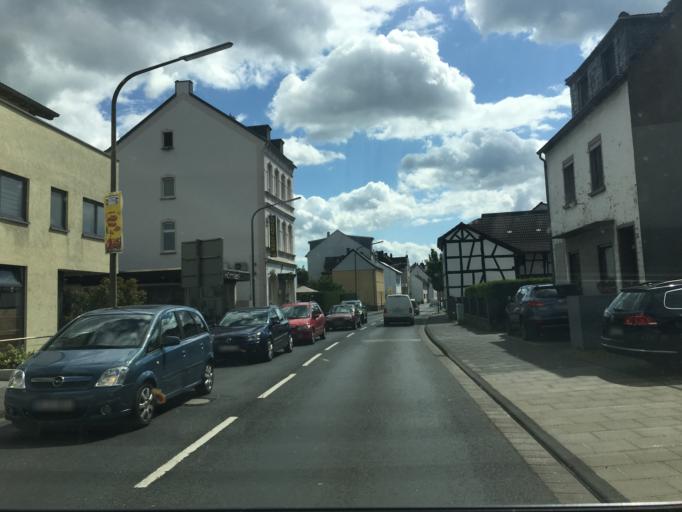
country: DE
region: Rheinland-Pfalz
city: Bad Neuenahr-Ahrweiler
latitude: 50.5453
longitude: 7.1216
